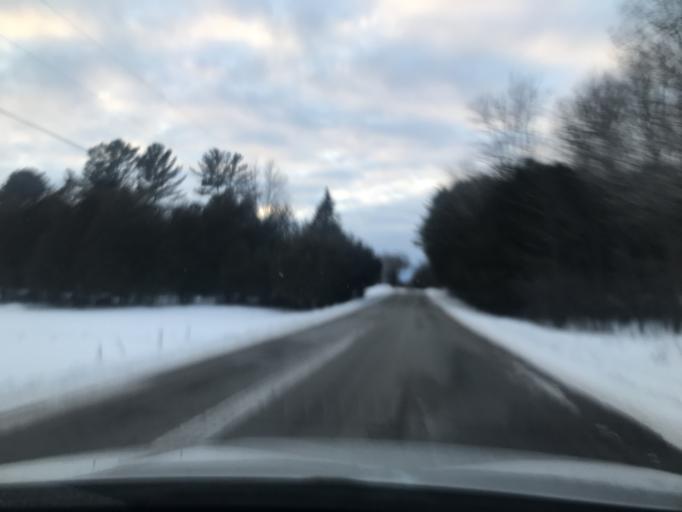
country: US
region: Wisconsin
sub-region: Marinette County
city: Peshtigo
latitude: 45.1644
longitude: -87.7340
